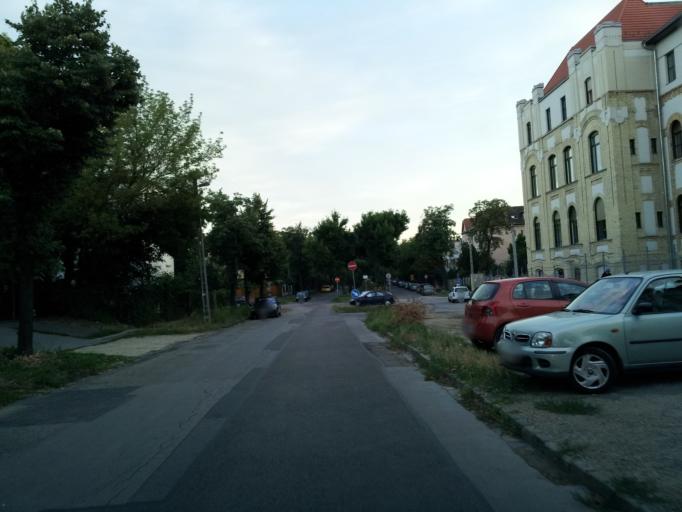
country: HU
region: Budapest
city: Budapest XIV. keruelet
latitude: 47.5186
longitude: 19.1032
